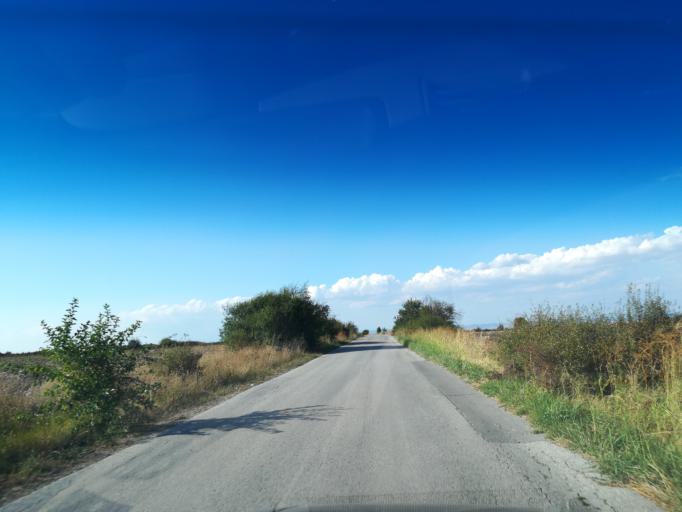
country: BG
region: Khaskovo
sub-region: Obshtina Mineralni Bani
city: Mineralni Bani
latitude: 42.0384
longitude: 25.2833
